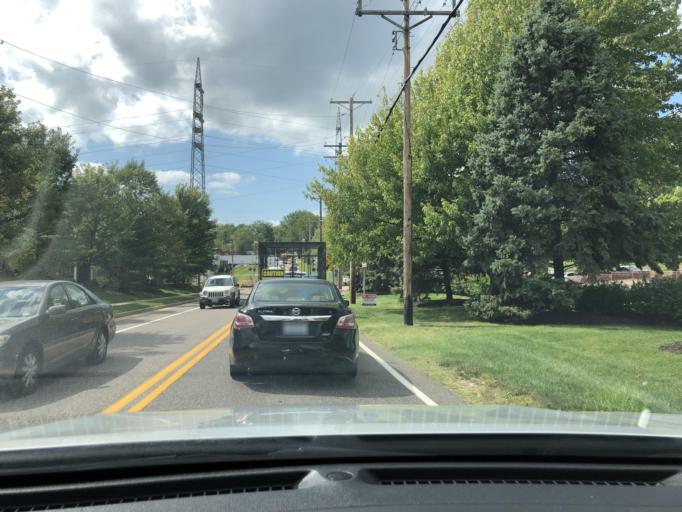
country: US
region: Missouri
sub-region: Saint Louis County
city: Affton
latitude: 38.5438
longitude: -90.3255
